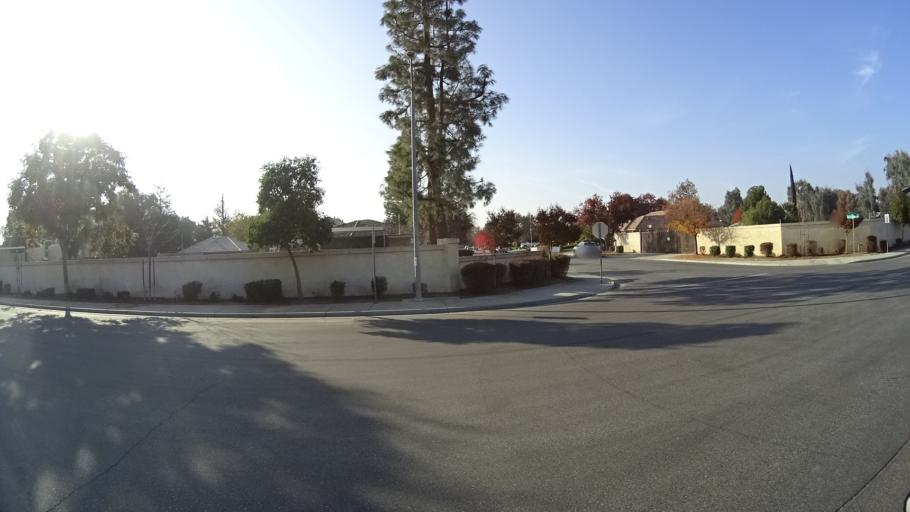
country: US
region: California
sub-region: Kern County
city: Rosedale
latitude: 35.3585
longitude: -119.1544
